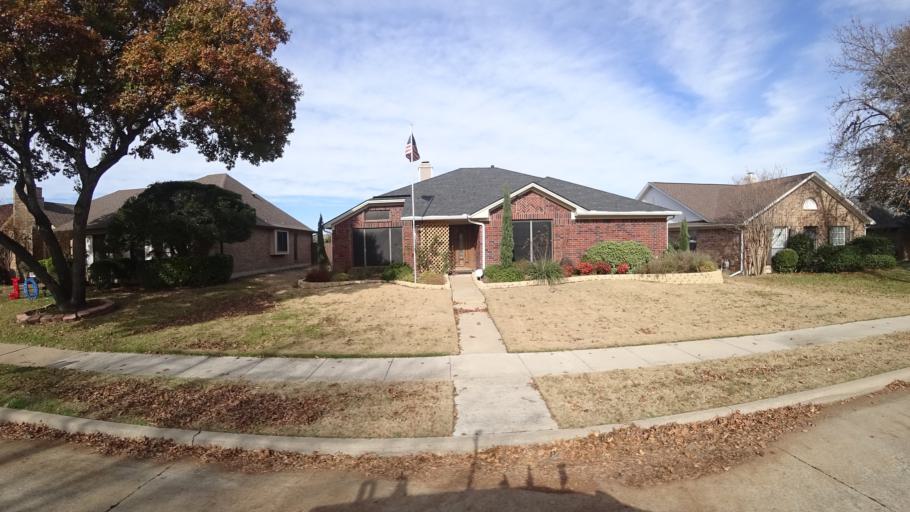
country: US
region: Texas
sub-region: Denton County
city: Highland Village
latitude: 33.0621
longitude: -97.0370
